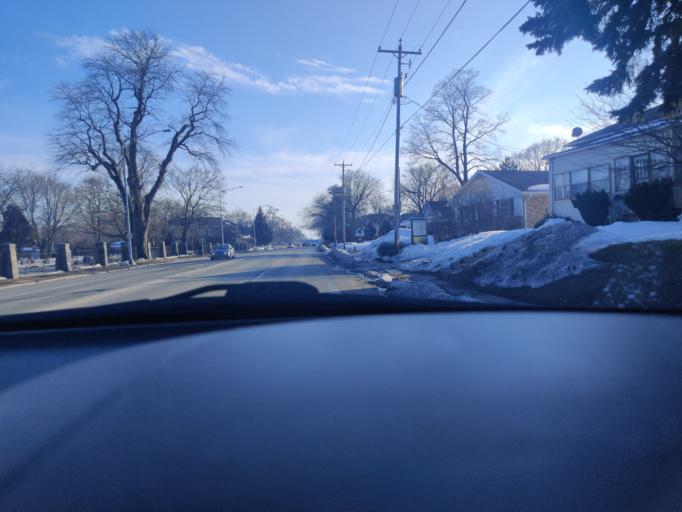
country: US
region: Wisconsin
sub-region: Kenosha County
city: Kenosha
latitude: 42.5736
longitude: -87.8226
